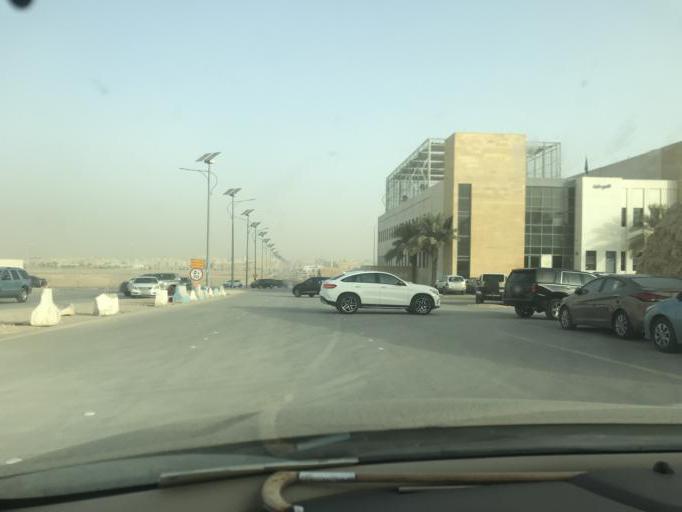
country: SA
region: Ar Riyad
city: Riyadh
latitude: 24.8418
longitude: 46.6663
